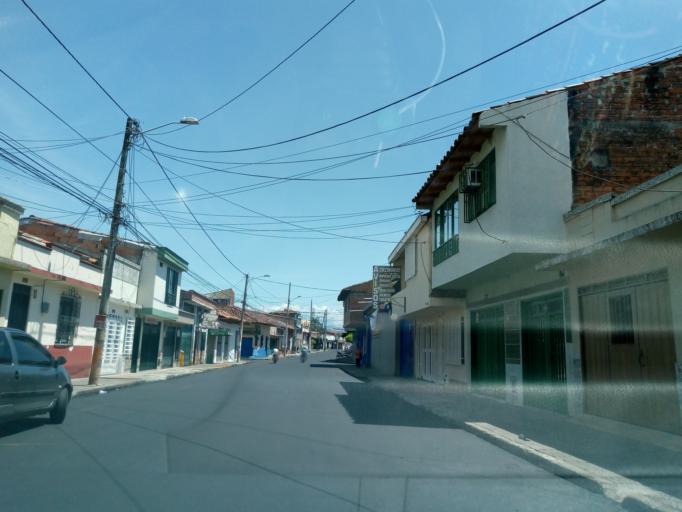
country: CO
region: Valle del Cauca
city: Cartago
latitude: 4.7439
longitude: -75.9121
